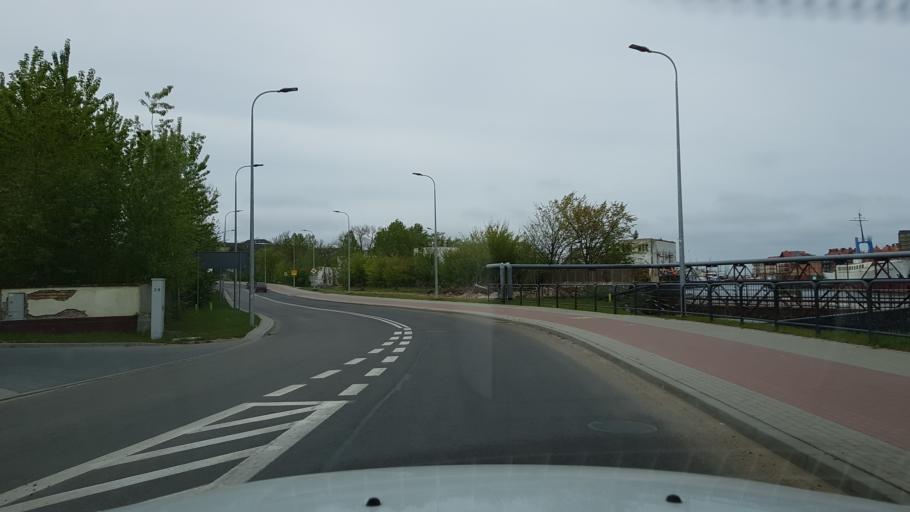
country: PL
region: Pomeranian Voivodeship
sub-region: Powiat slupski
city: Ustka
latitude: 54.5798
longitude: 16.8567
